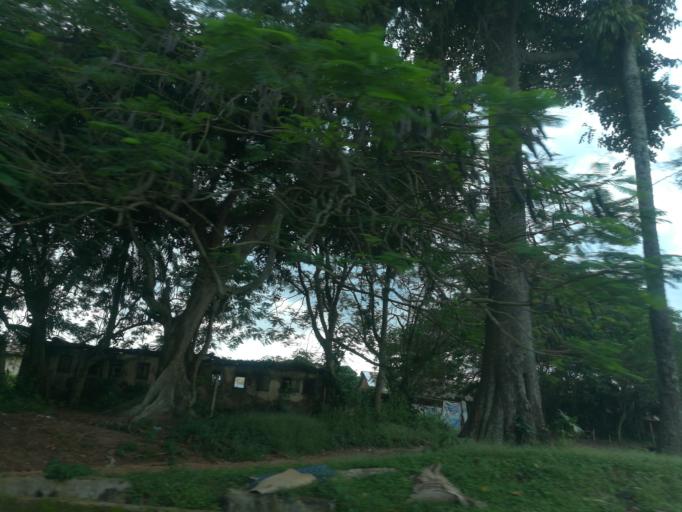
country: NG
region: Oyo
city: Ibadan
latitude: 7.4519
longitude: 3.9004
